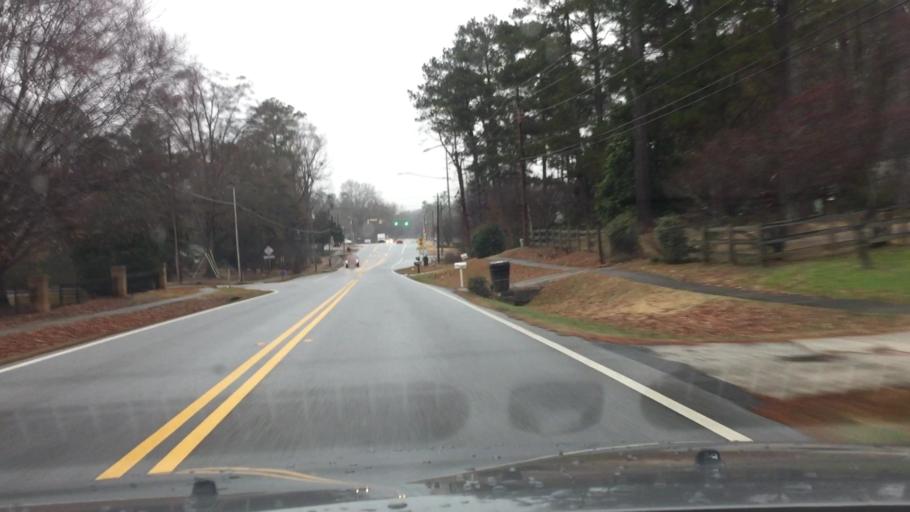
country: US
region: Georgia
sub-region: Cobb County
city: Powder Springs
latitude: 33.8708
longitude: -84.6759
